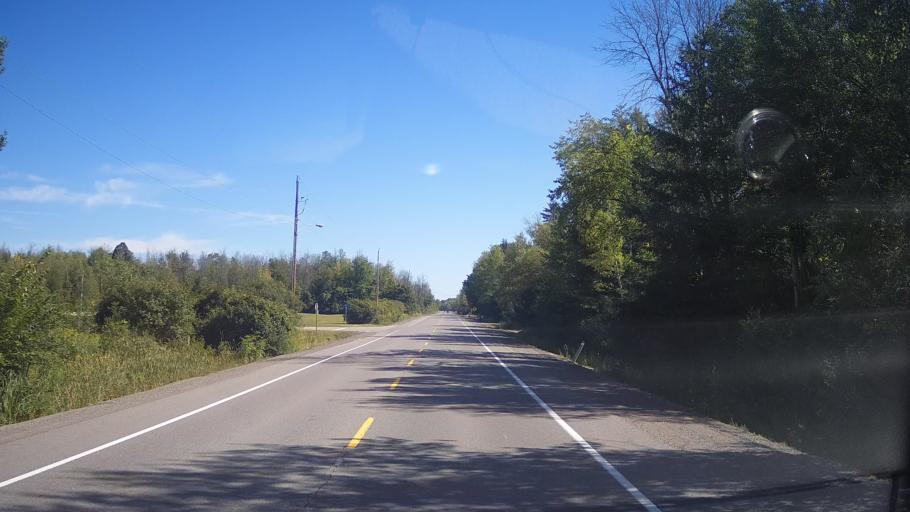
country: CA
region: Ontario
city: Bells Corners
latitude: 45.0648
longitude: -75.6631
